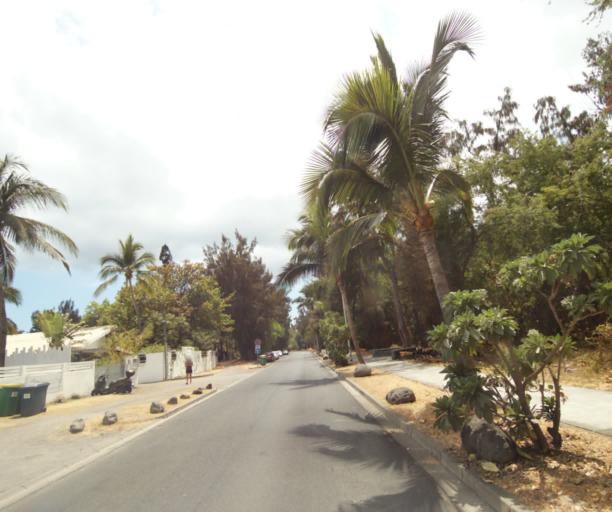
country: RE
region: Reunion
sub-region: Reunion
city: Saint-Paul
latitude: -21.0643
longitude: 55.2225
